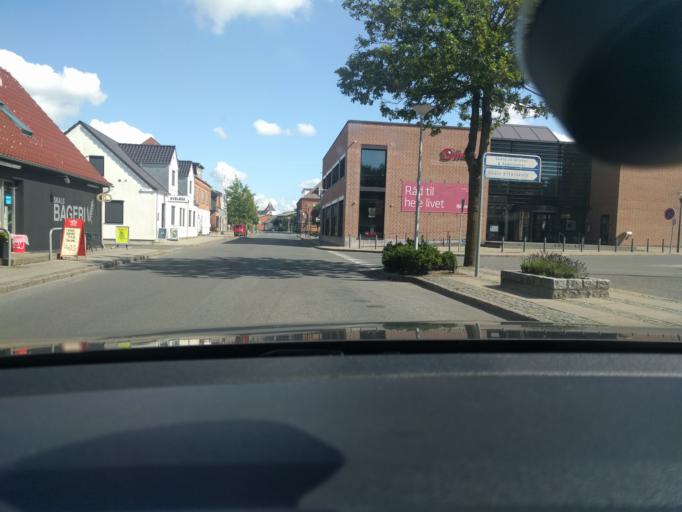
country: DK
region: Central Jutland
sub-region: Viborg Kommune
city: Viborg
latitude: 56.5552
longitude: 9.4028
